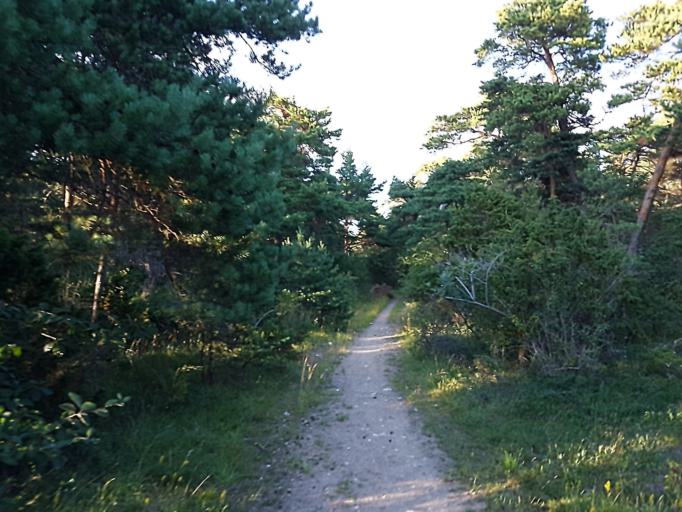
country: SE
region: Gotland
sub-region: Gotland
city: Visby
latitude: 57.6201
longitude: 18.3388
